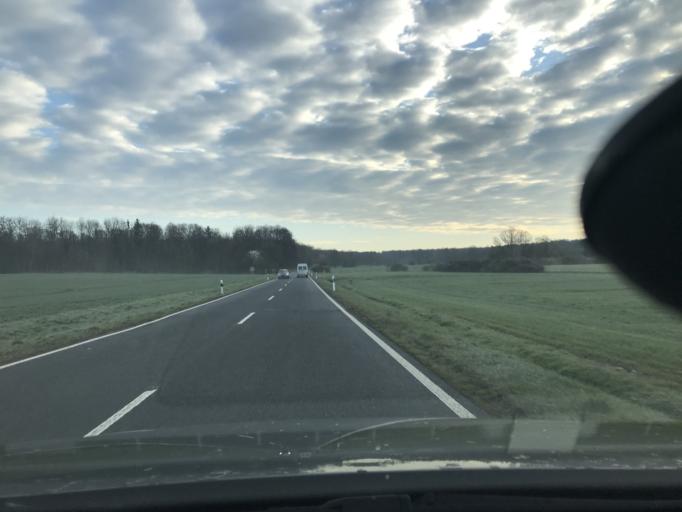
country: DE
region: Thuringia
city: Menteroda
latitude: 51.2798
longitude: 10.5360
